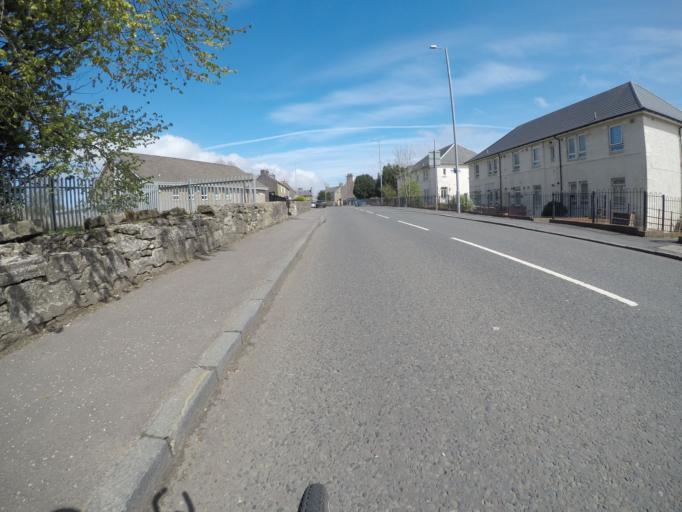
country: GB
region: Scotland
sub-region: East Ayrshire
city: Stewarton
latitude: 55.6782
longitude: -4.5191
